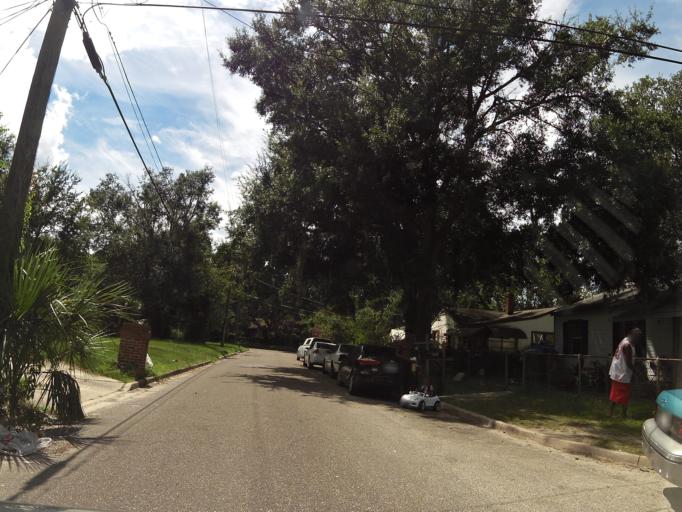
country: US
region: Florida
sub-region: Duval County
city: Jacksonville
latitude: 30.3837
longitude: -81.6441
